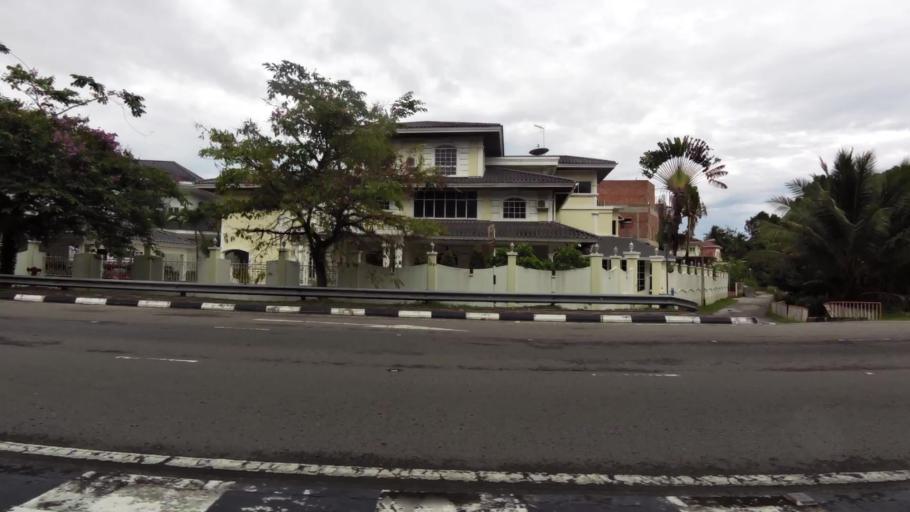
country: BN
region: Brunei and Muara
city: Bandar Seri Begawan
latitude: 4.9031
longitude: 114.9394
